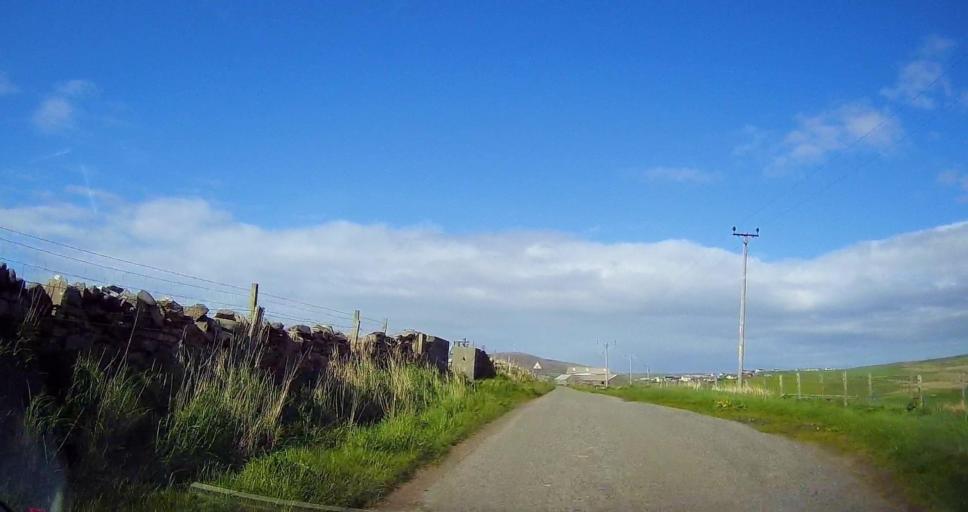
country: GB
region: Scotland
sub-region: Shetland Islands
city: Sandwick
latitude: 59.9051
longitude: -1.3358
